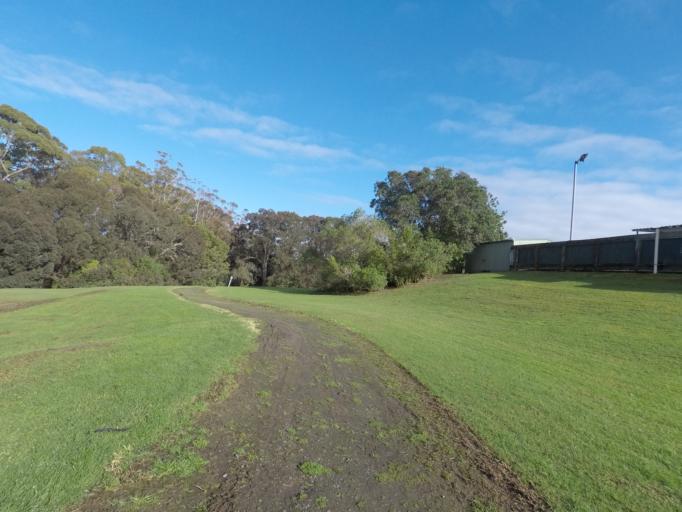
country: NZ
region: Auckland
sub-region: Auckland
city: Warkworth
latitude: -36.4218
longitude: 174.7223
